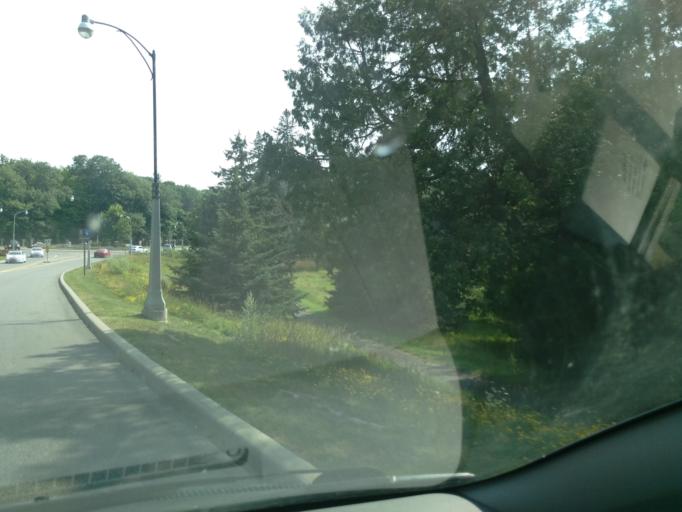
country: CA
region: Quebec
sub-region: Outaouais
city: Gatineau
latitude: 45.4473
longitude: -75.6891
